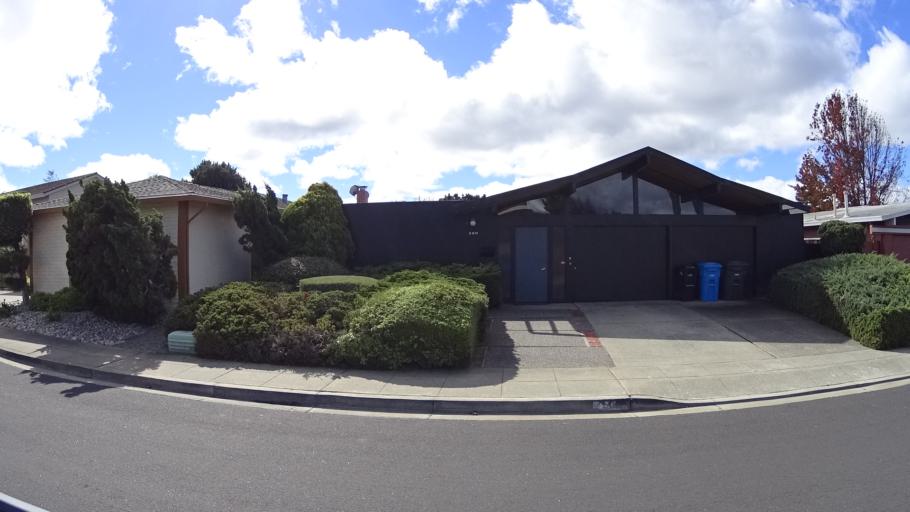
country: US
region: California
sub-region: San Mateo County
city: Foster City
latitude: 37.5672
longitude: -122.2534
